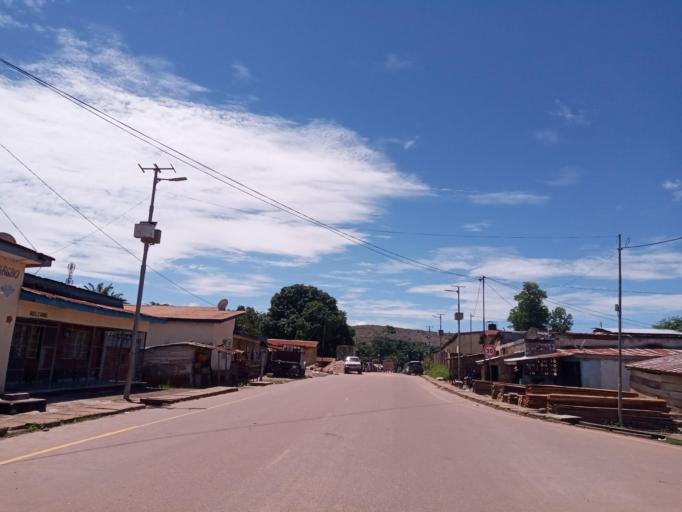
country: SL
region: Eastern Province
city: Koidu
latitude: 8.6408
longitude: -10.9701
